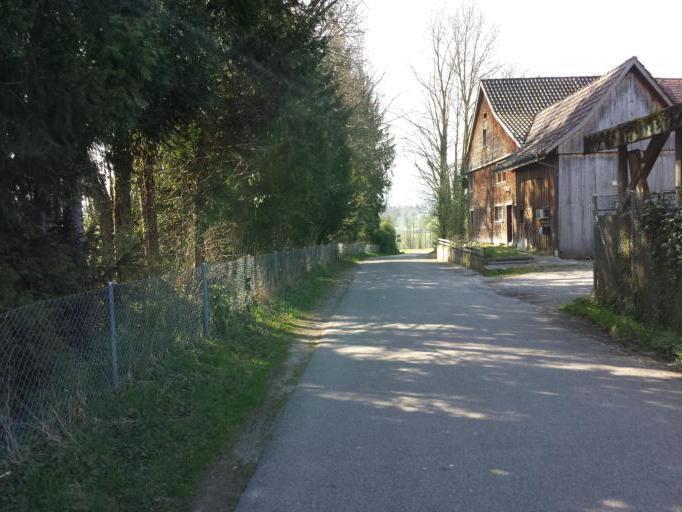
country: CH
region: Thurgau
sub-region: Arbon District
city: Salmsach
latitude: 47.5442
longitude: 9.3484
